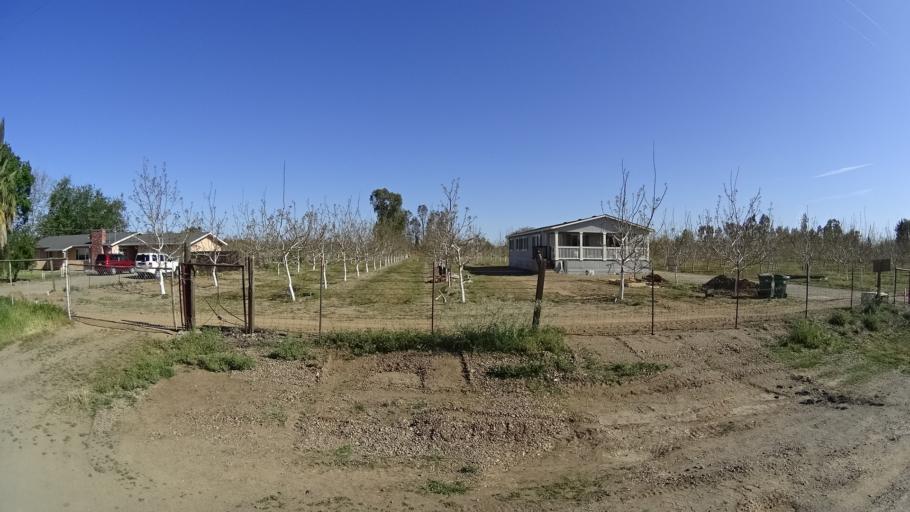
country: US
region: California
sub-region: Glenn County
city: Orland
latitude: 39.7150
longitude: -122.2017
